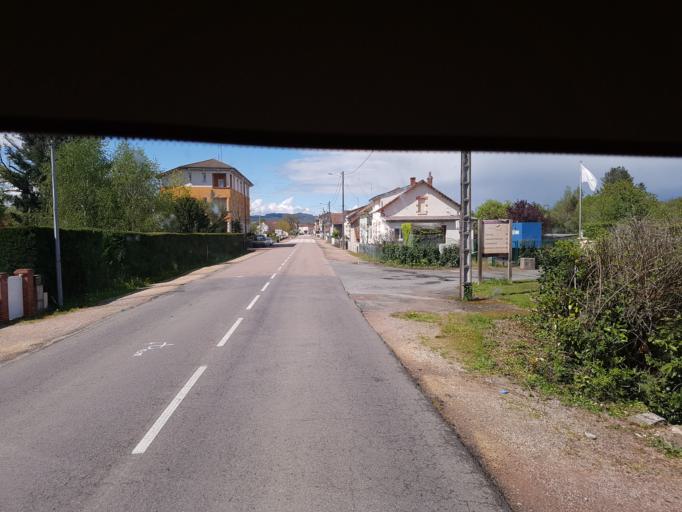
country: FR
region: Bourgogne
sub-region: Departement de Saone-et-Loire
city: Etang-sur-Arroux
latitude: 46.8632
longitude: 4.1912
